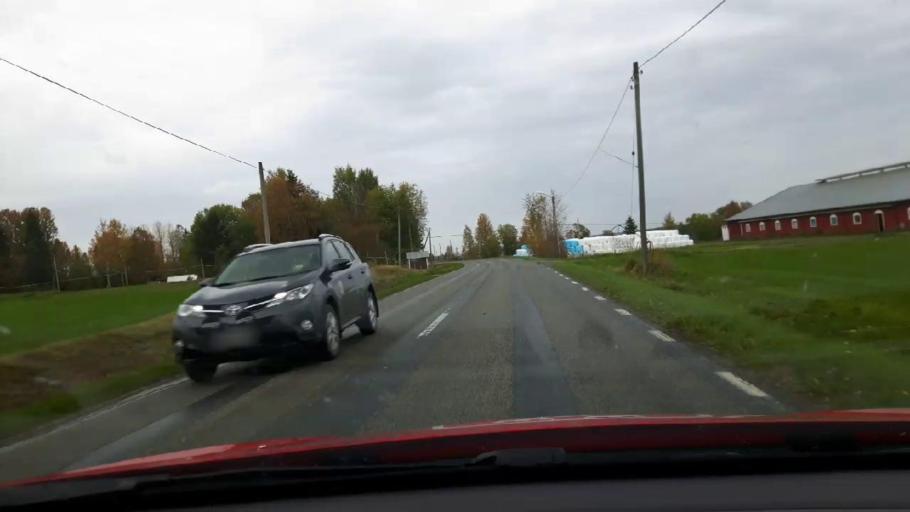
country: SE
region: Jaemtland
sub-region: Bergs Kommun
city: Hoverberg
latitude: 62.8489
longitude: 14.3828
